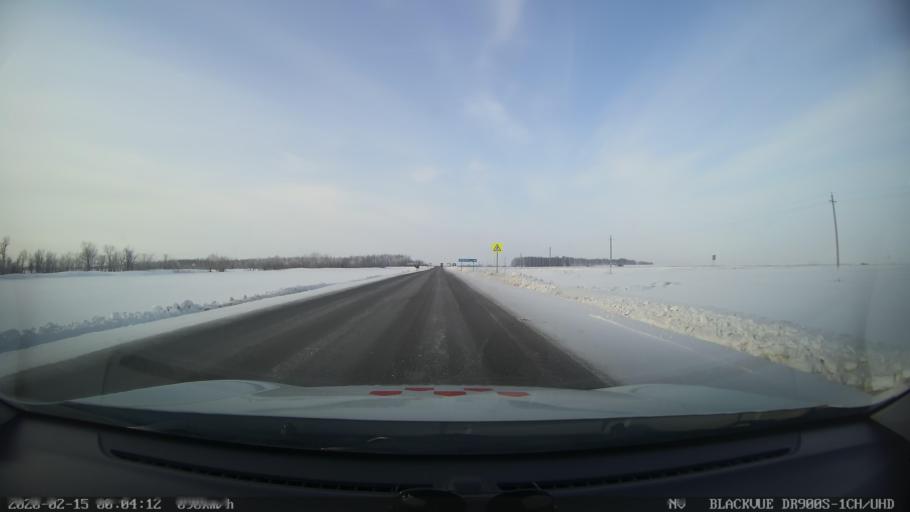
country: RU
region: Tatarstan
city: Kuybyshevskiy Zaton
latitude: 55.3799
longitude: 48.9869
